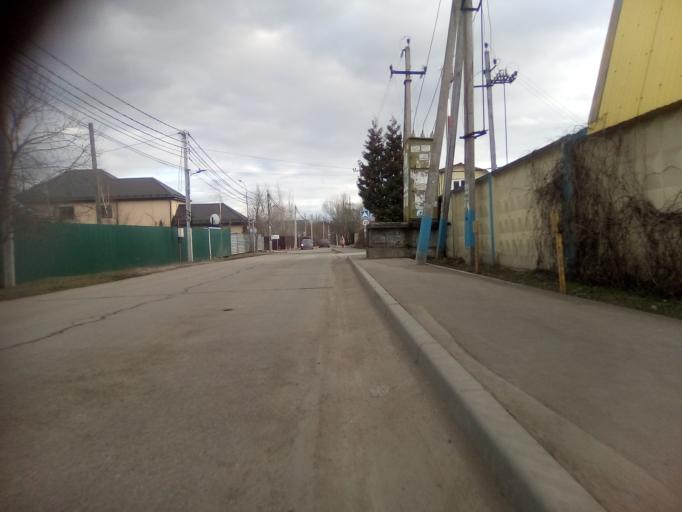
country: RU
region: Moskovskaya
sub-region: Leninskiy Rayon
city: Vnukovo
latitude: 55.5926
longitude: 37.3201
